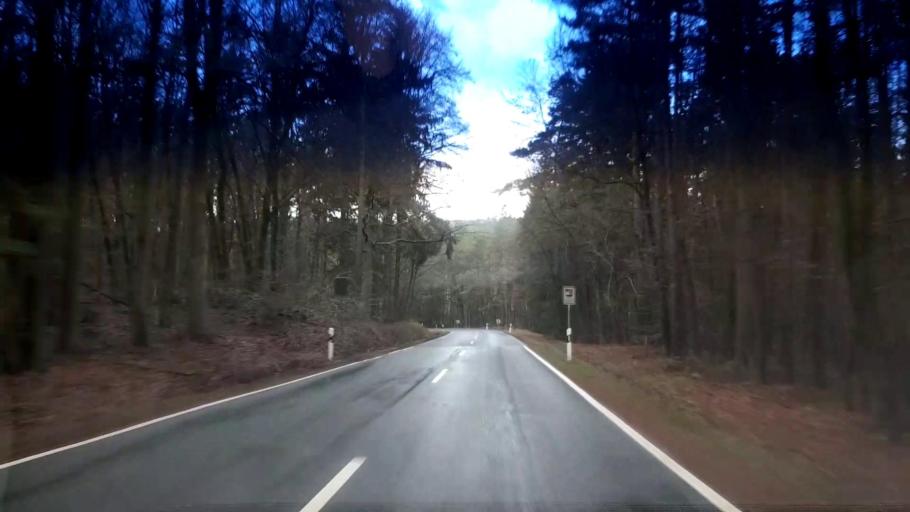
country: DE
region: Bavaria
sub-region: Upper Franconia
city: Lauter
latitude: 49.9667
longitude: 10.7599
